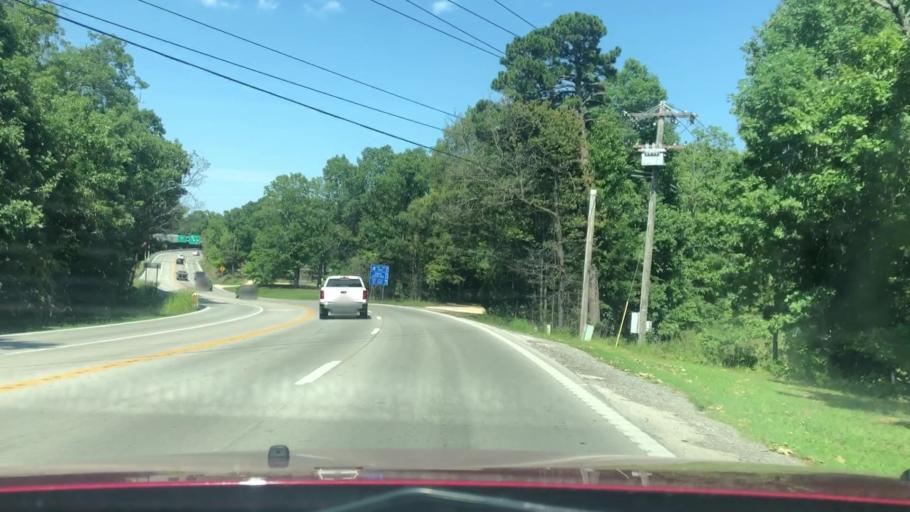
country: US
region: Missouri
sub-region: Stone County
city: Kimberling City
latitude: 36.6723
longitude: -93.3309
